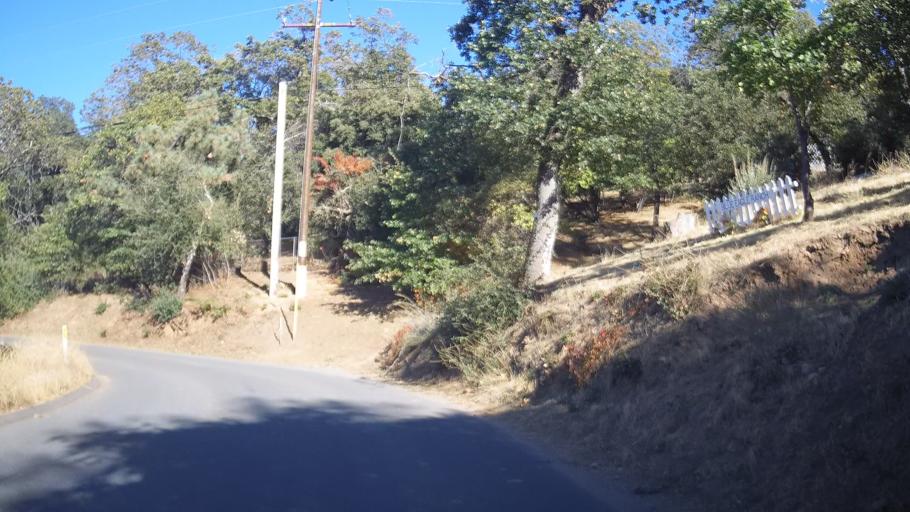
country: US
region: California
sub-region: San Diego County
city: Julian
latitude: 33.0509
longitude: -116.6338
